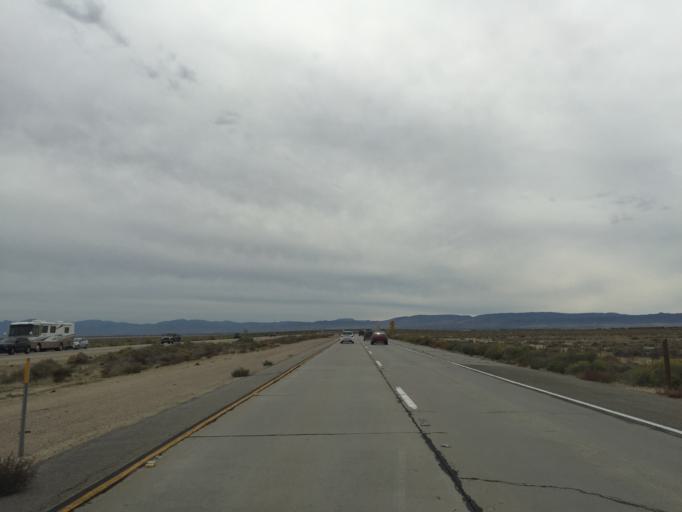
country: US
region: California
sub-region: Kern County
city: Rosamond
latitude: 34.8152
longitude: -118.1708
